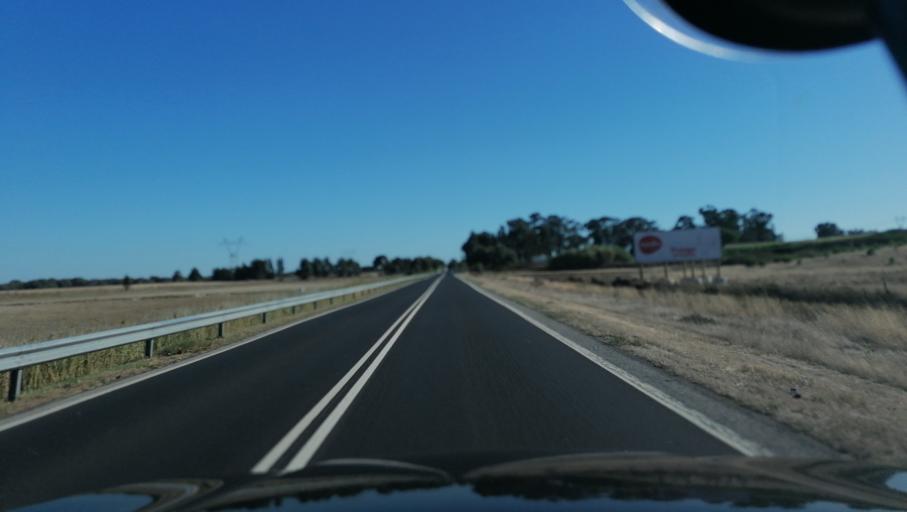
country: PT
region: Santarem
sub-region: Benavente
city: Samora Correia
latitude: 38.8690
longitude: -8.8812
